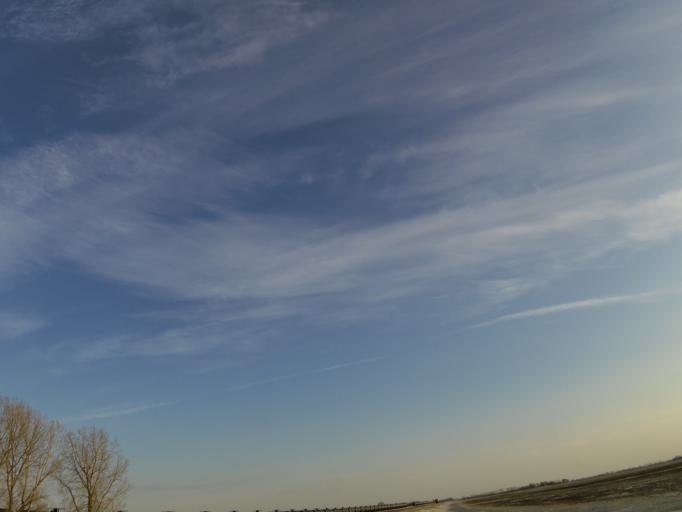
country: US
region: North Dakota
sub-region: Walsh County
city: Grafton
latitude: 48.5052
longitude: -97.4380
